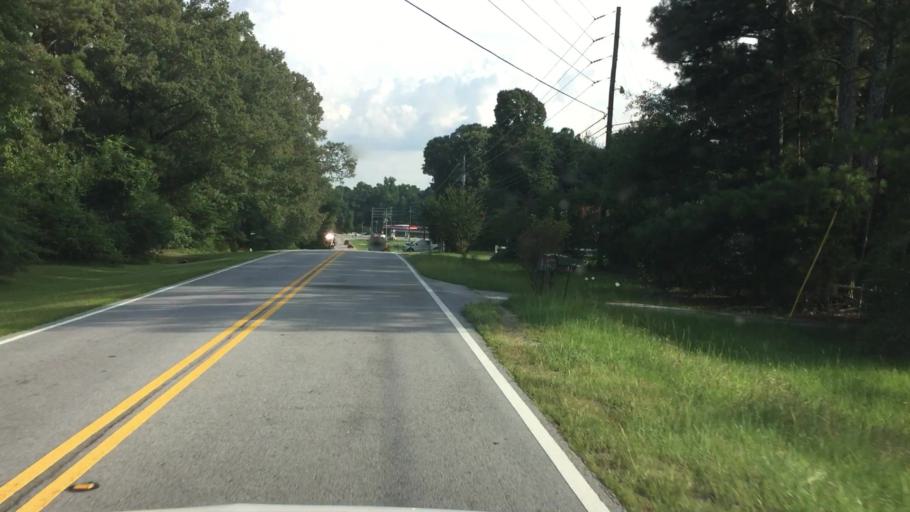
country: US
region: Georgia
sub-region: DeKalb County
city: Pine Mountain
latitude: 33.6109
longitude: -84.1369
